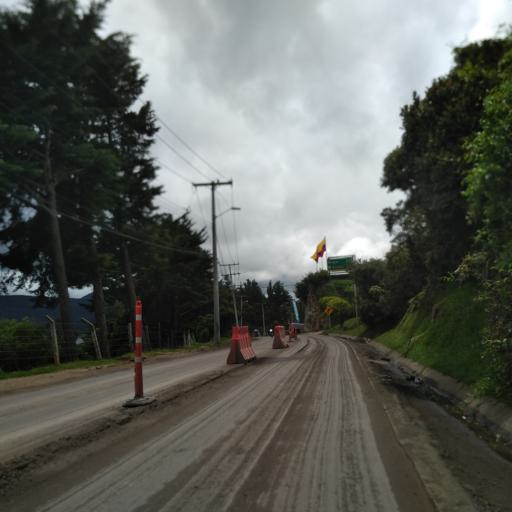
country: CO
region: Cundinamarca
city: La Calera
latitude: 4.6924
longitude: -73.9873
